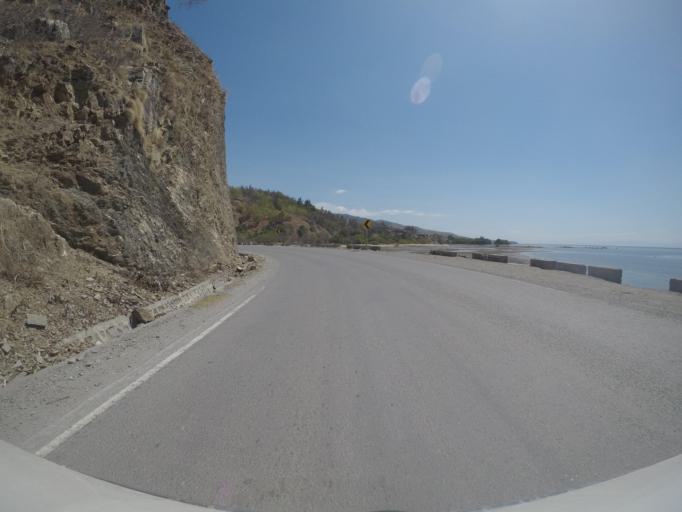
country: TL
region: Dili
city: Dili
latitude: -8.5680
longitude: 125.4706
